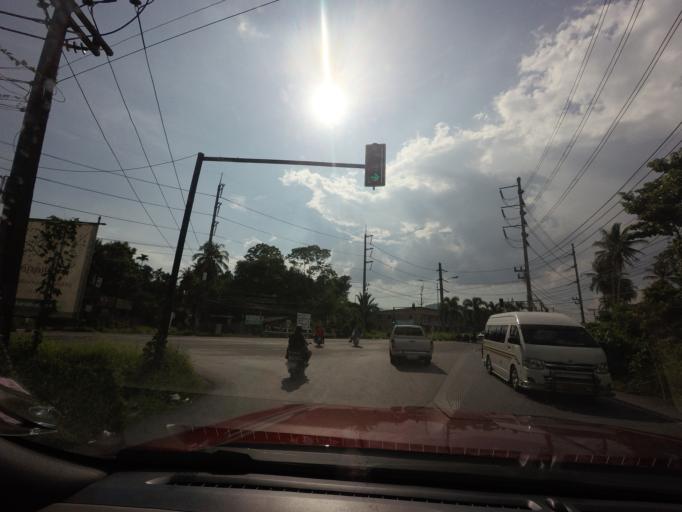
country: TH
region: Yala
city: Yala
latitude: 6.5747
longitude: 101.1996
